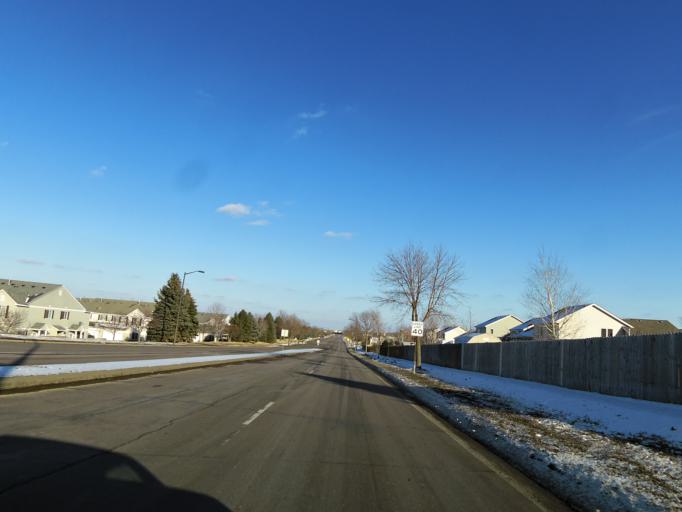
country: US
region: Minnesota
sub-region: Scott County
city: Shakopee
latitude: 44.7736
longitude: -93.5001
